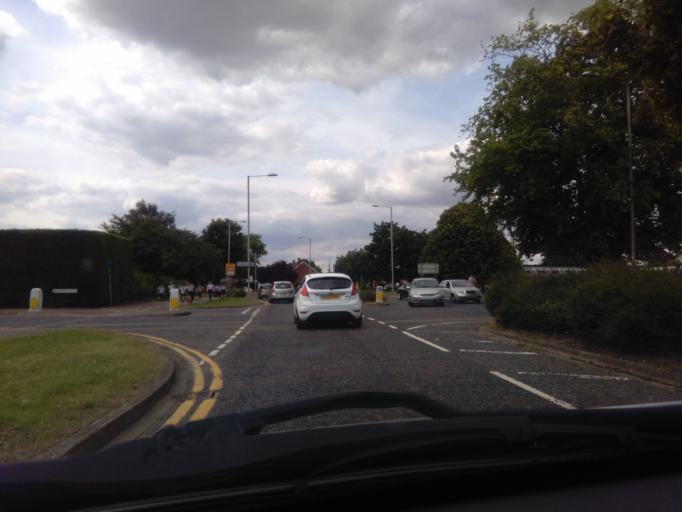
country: GB
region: England
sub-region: Bedford
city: Bedford
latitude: 52.1439
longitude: -0.4447
